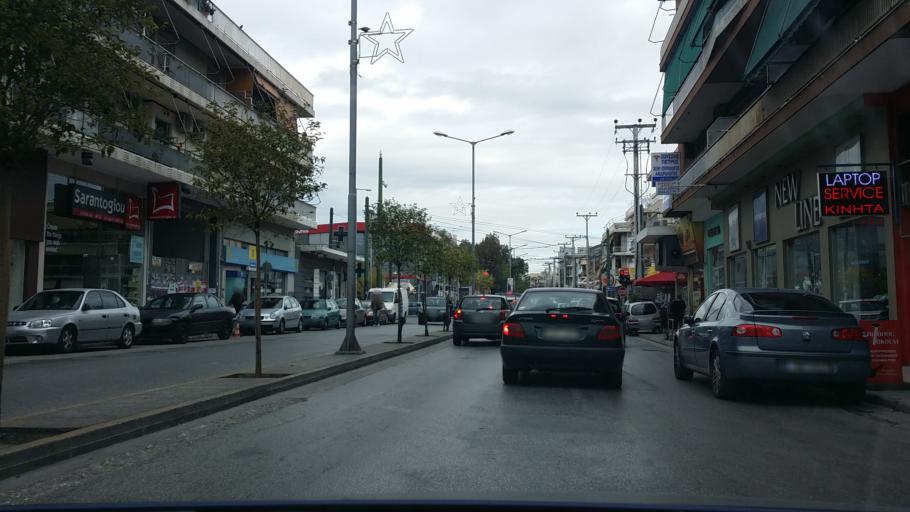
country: GR
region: Attica
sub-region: Nomarchia Athinas
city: Peristeri
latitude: 38.0160
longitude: 23.6913
